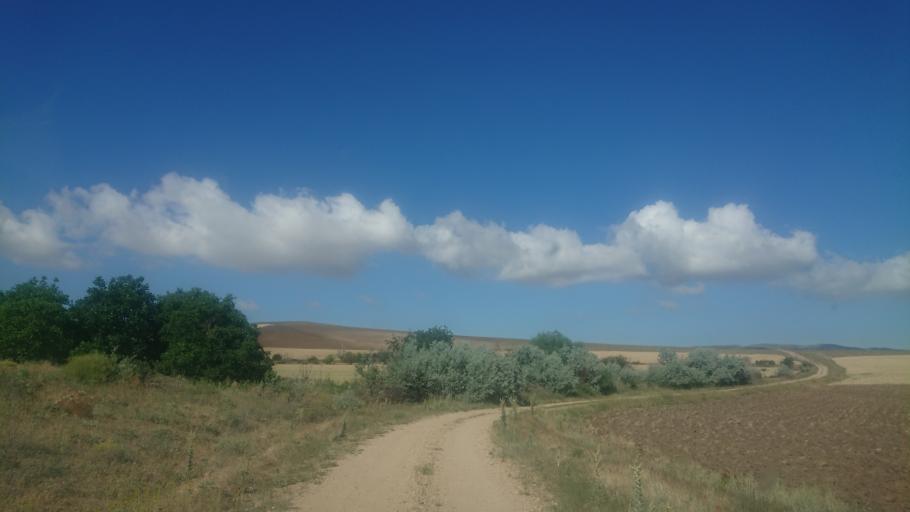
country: TR
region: Aksaray
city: Agacoren
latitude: 38.9102
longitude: 33.8780
